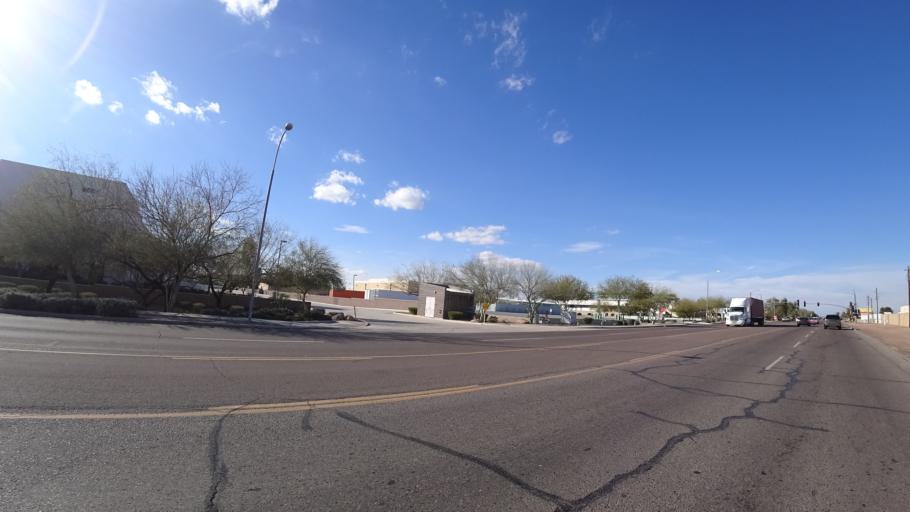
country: US
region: Arizona
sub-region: Maricopa County
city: Tolleson
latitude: 33.4395
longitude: -112.2382
